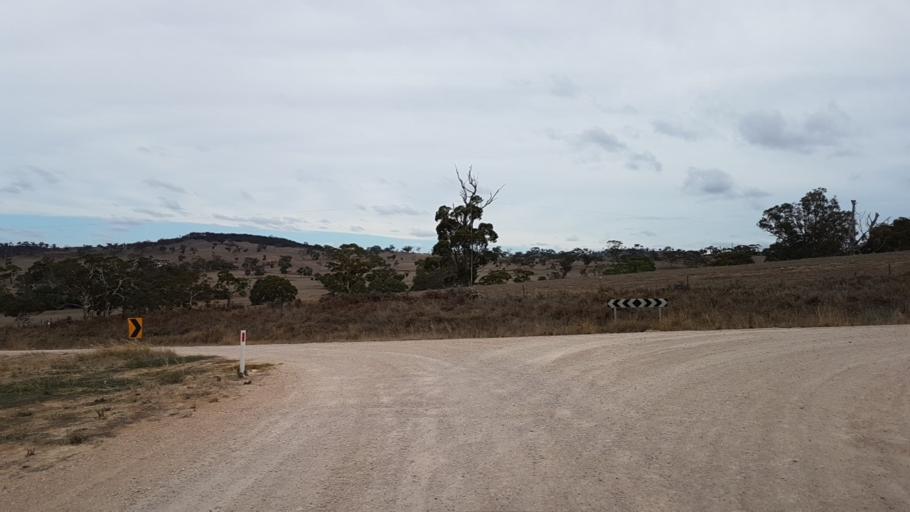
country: AU
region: South Australia
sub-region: Adelaide Hills
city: Birdwood
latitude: -34.9175
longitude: 139.0706
